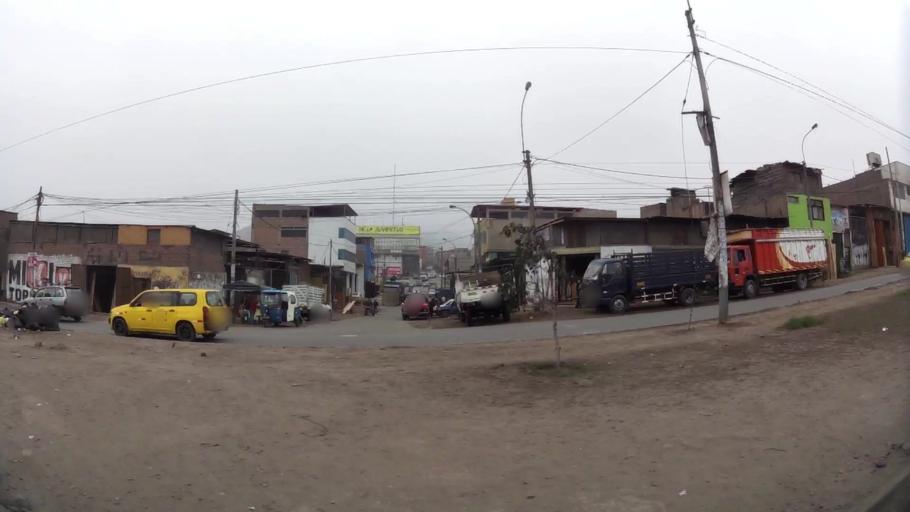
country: PE
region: Lima
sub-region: Lima
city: Surco
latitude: -12.1645
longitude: -76.9534
